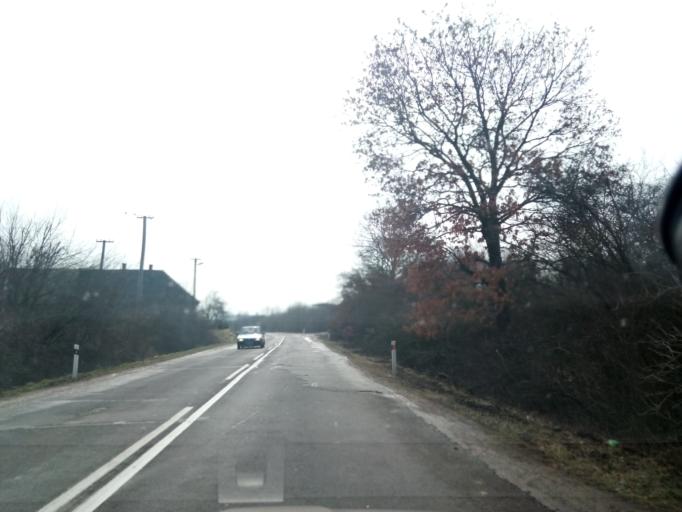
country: SK
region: Kosicky
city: Secovce
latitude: 48.6242
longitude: 21.5886
